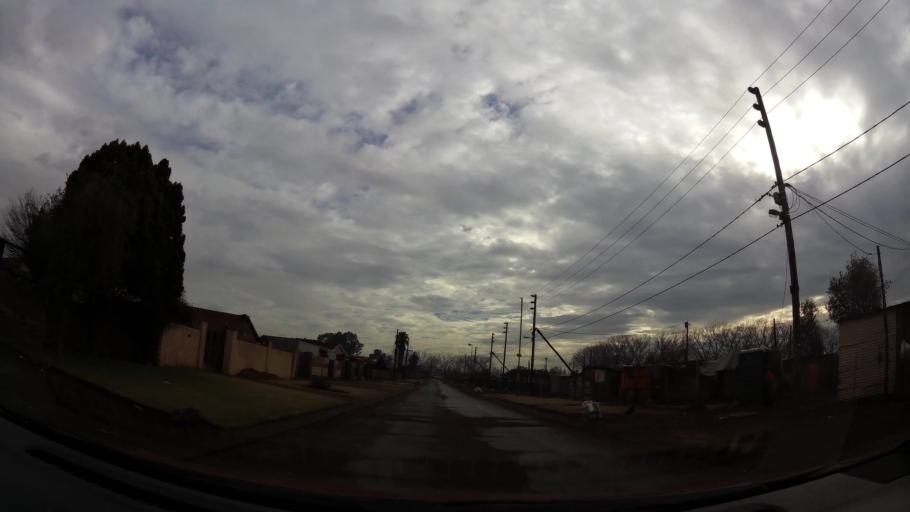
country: ZA
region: Gauteng
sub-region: City of Johannesburg Metropolitan Municipality
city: Soweto
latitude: -26.2900
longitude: 27.8408
